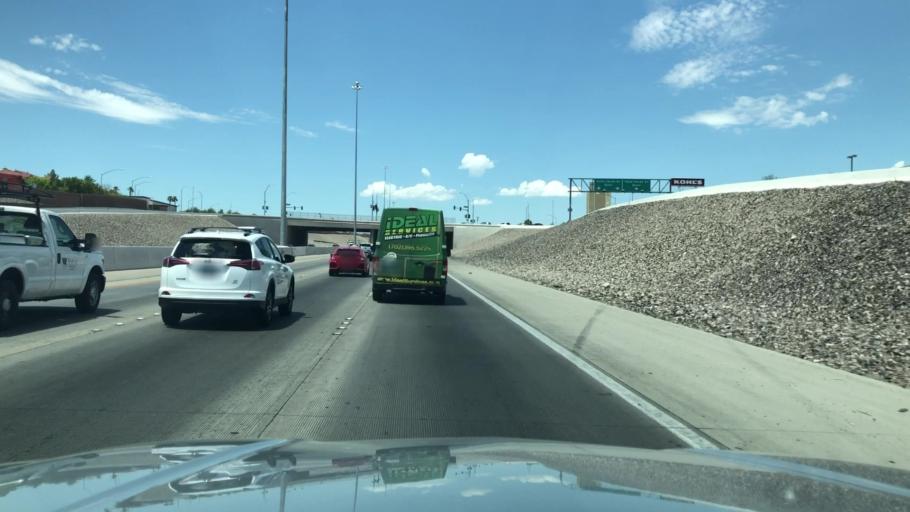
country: US
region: Nevada
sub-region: Clark County
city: Whitney
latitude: 36.0280
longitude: -115.0595
